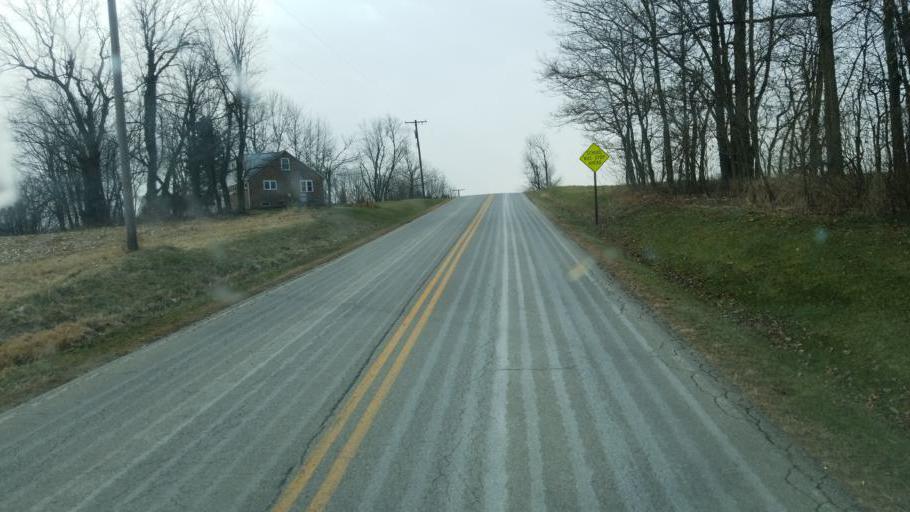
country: US
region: Ohio
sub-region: Richland County
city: Lexington
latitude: 40.6835
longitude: -82.5303
